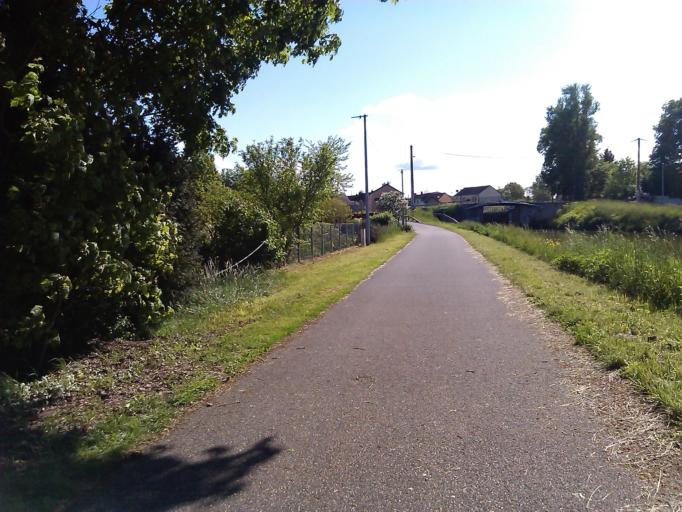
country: FR
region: Bourgogne
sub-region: Departement de Saone-et-Loire
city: Ecuisses
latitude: 46.7629
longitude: 4.5223
